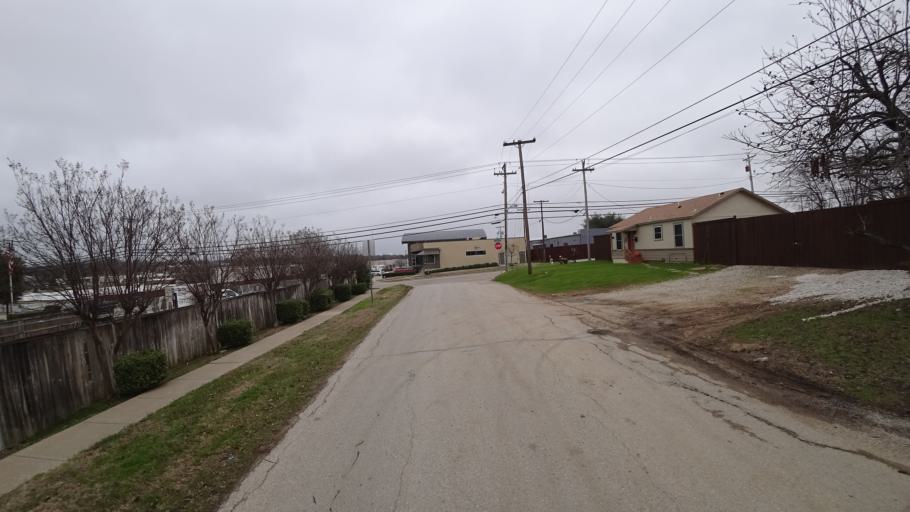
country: US
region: Texas
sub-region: Denton County
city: Lewisville
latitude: 33.0550
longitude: -97.0019
